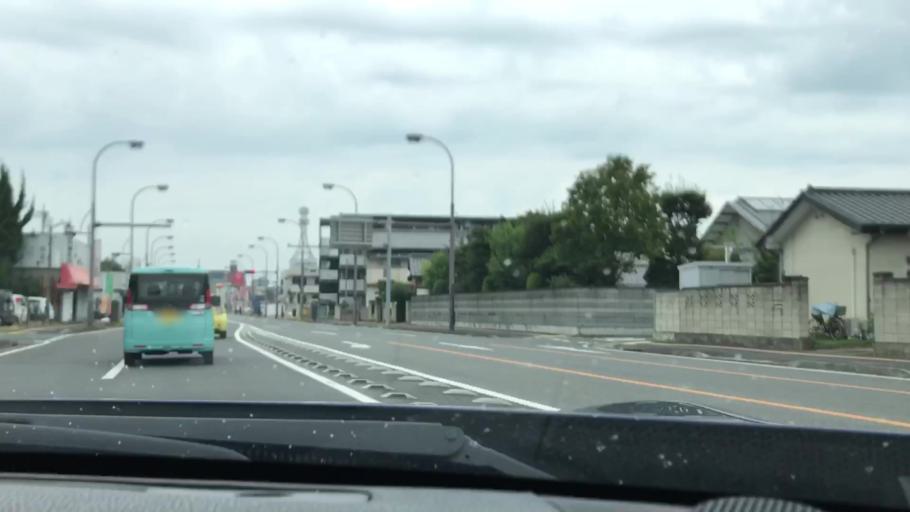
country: JP
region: Gunma
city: Maebashi-shi
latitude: 36.3763
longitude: 139.0703
